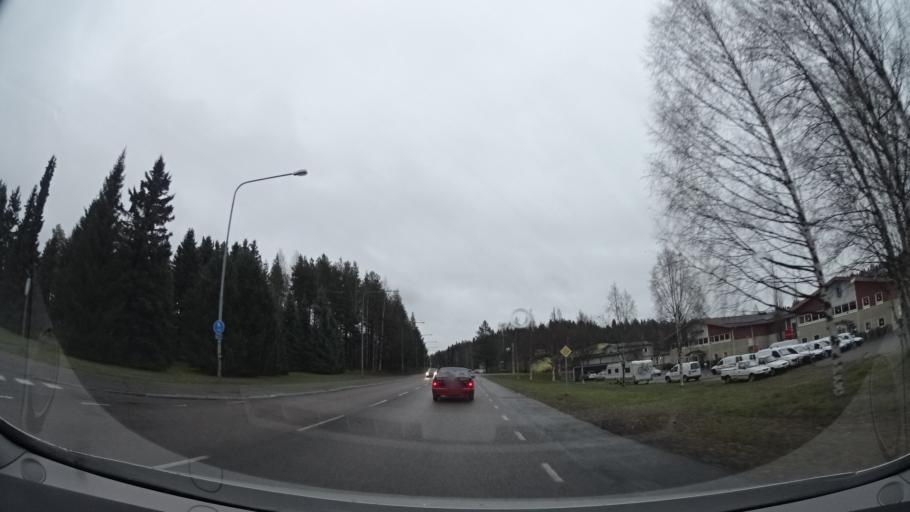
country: SE
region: Vaesterbotten
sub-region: Skelleftea Kommun
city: Skelleftea
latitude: 64.7569
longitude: 20.9772
